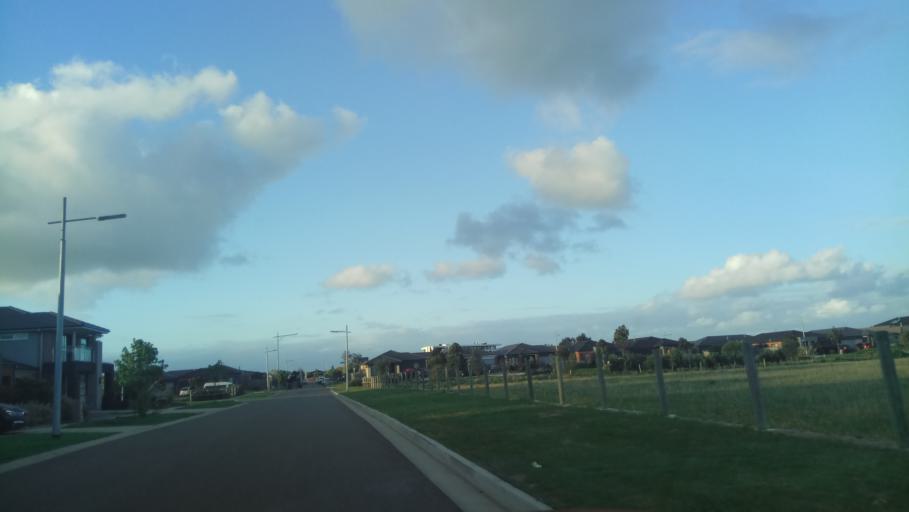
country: AU
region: Victoria
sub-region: Wyndham
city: Point Cook
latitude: -37.9151
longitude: 144.7699
